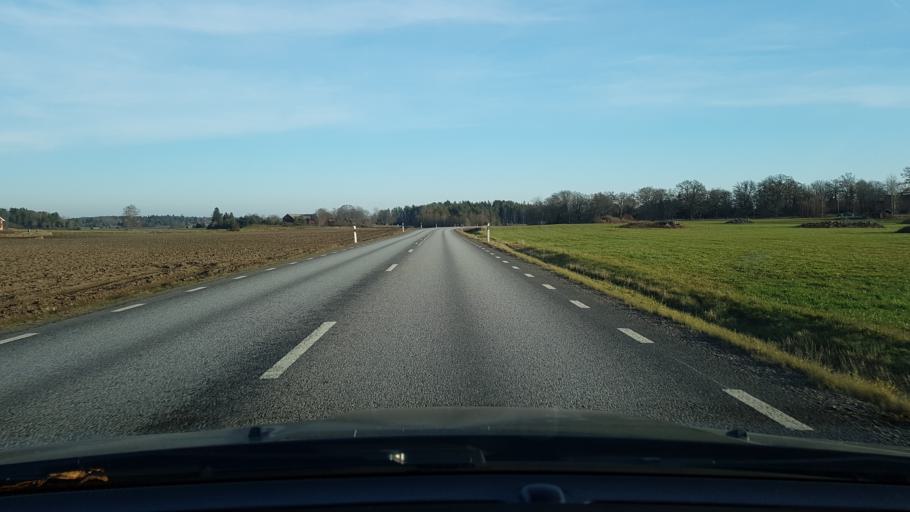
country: SE
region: Stockholm
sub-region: Sigtuna Kommun
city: Marsta
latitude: 59.7529
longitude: 18.0253
